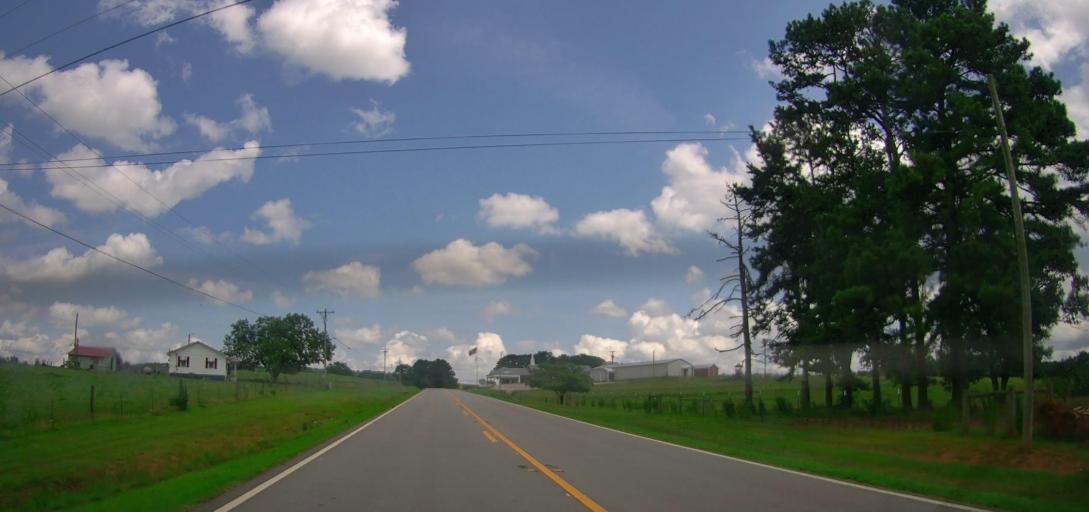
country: US
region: Georgia
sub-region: Carroll County
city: Bowdon
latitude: 33.4449
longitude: -85.2845
